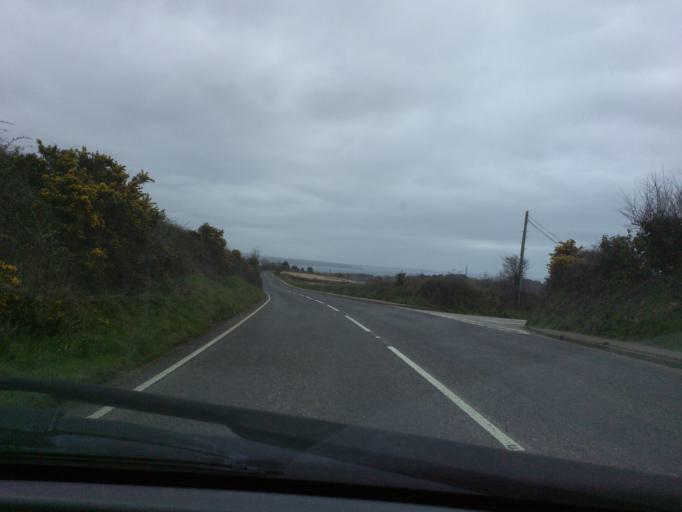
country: GB
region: England
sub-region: Cornwall
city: Penzance
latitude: 50.1163
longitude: -5.5697
